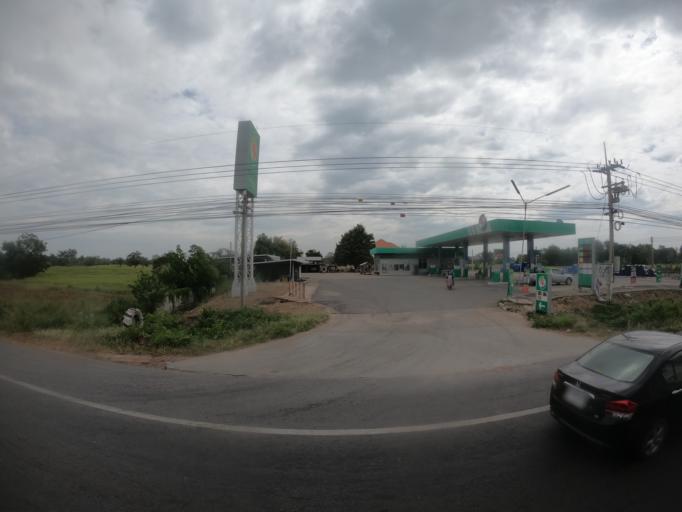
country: TH
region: Maha Sarakham
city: Kantharawichai
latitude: 16.2931
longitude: 103.2954
